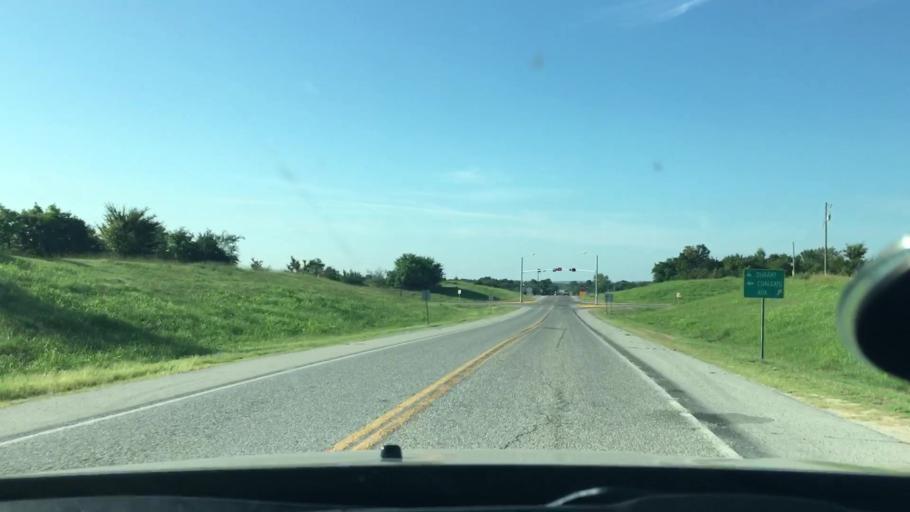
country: US
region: Oklahoma
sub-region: Coal County
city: Coalgate
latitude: 34.6127
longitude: -96.4244
